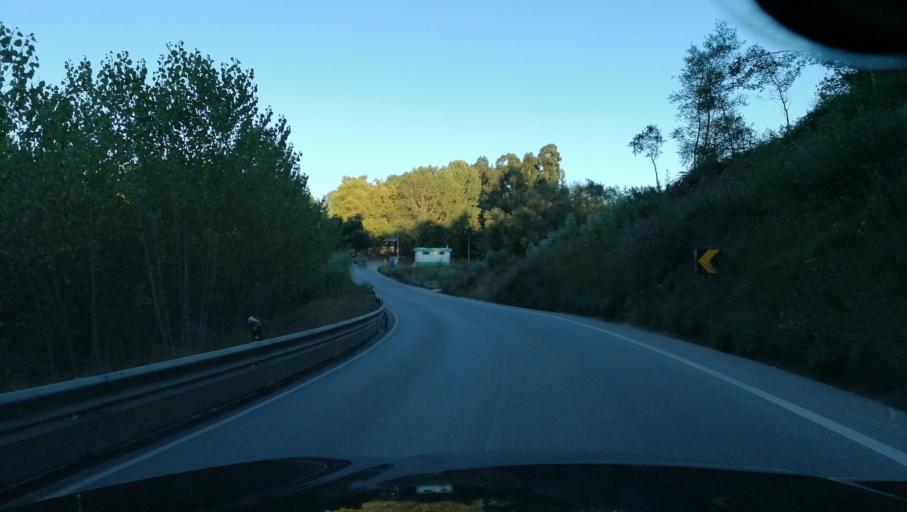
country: PT
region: Aveiro
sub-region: Agueda
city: Agueda
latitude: 40.5576
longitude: -8.4812
